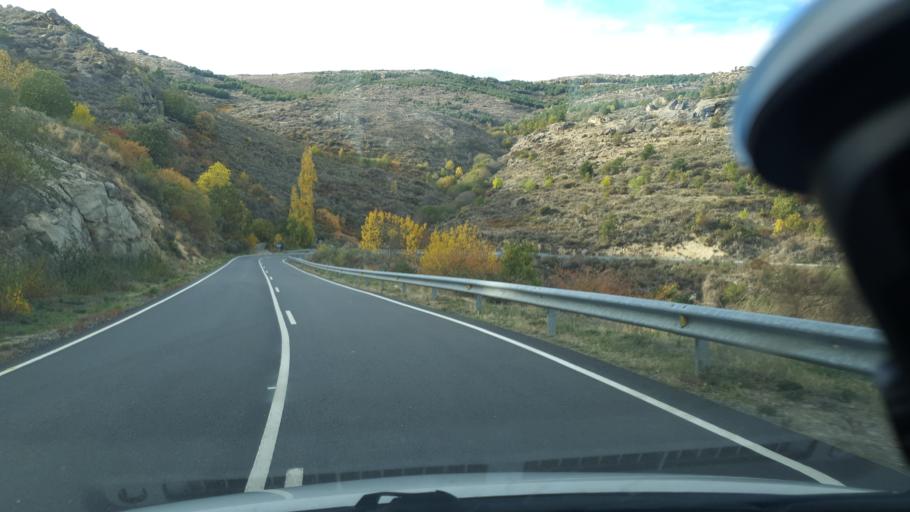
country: ES
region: Castille and Leon
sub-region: Provincia de Avila
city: Navaquesera
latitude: 40.4067
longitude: -4.9033
